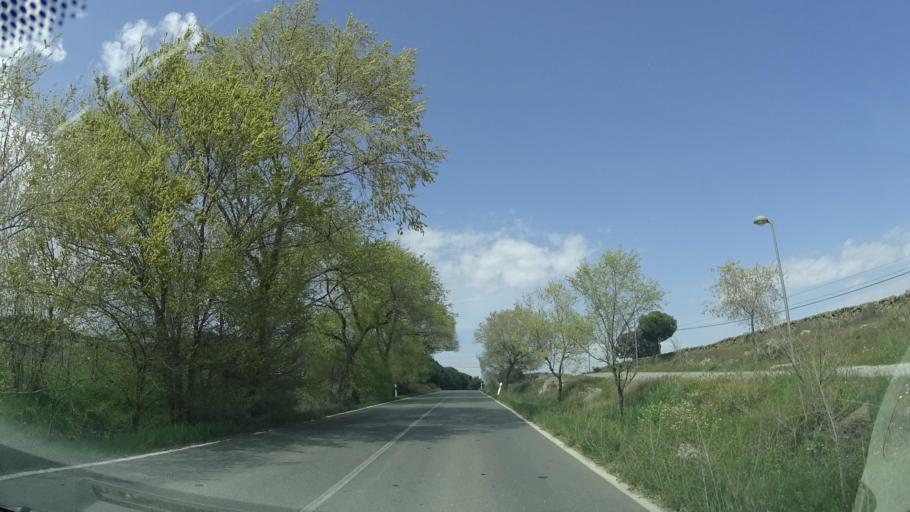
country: ES
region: Madrid
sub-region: Provincia de Madrid
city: Colmenar Viejo
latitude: 40.6858
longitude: -3.7695
